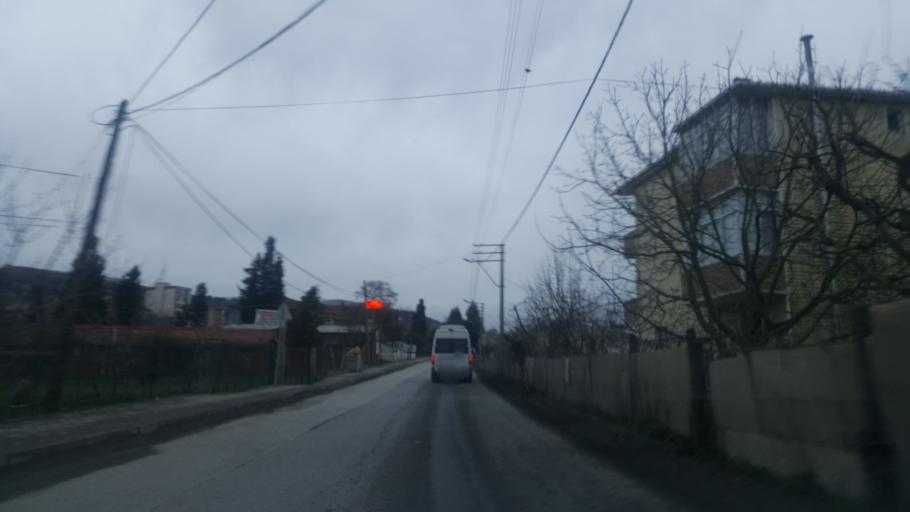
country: TR
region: Kocaeli
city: Tavsanli
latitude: 40.8492
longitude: 29.5550
